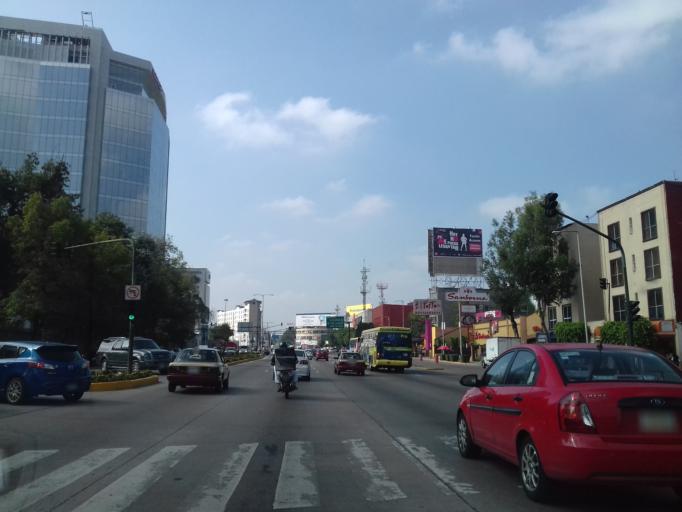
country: MX
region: Mexico City
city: Polanco
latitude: 19.4105
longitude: -99.1829
